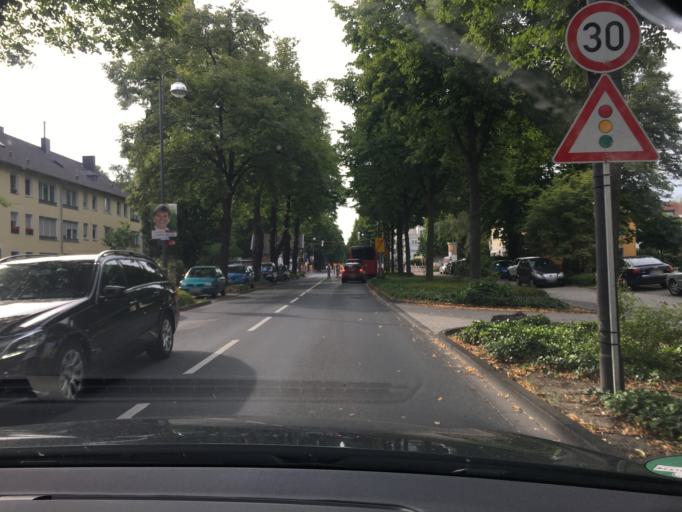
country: DE
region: North Rhine-Westphalia
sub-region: Regierungsbezirk Koln
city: Bonn
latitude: 50.7526
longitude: 7.0739
